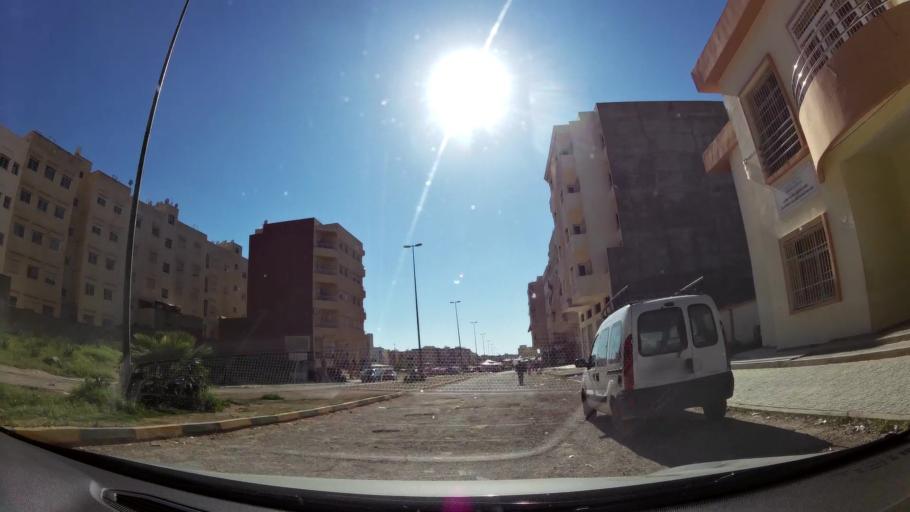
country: MA
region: Fes-Boulemane
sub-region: Fes
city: Fes
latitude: 34.0183
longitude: -4.9635
